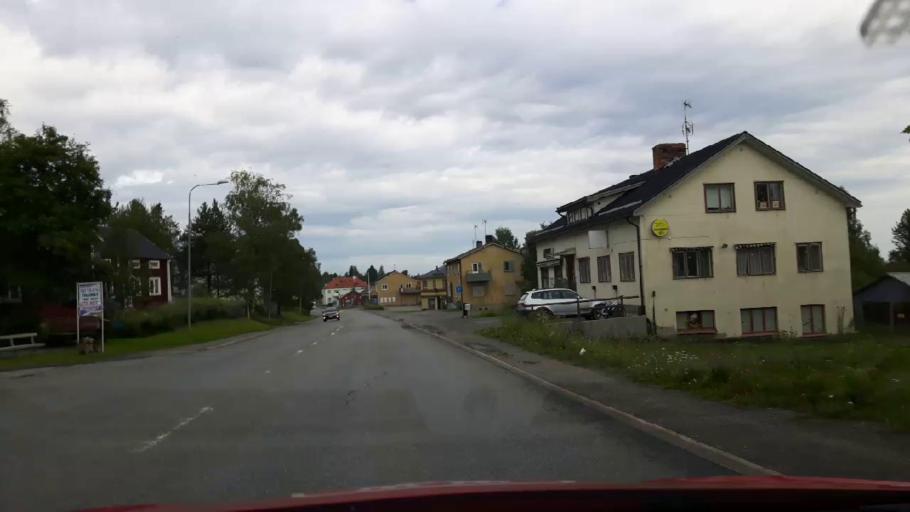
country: SE
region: Jaemtland
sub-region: Stroemsunds Kommun
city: Stroemsund
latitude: 63.5795
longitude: 15.3516
